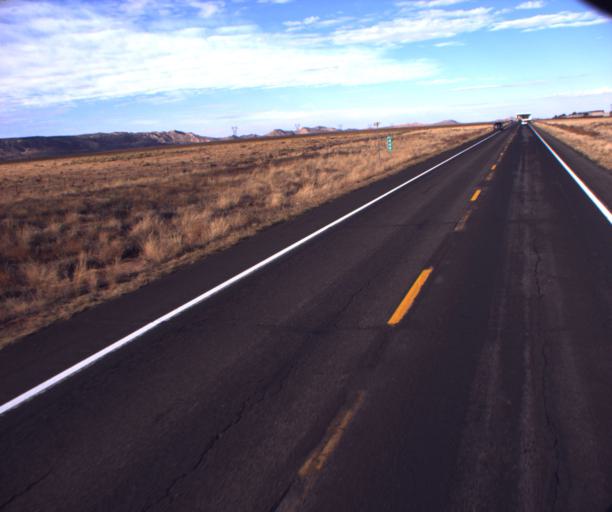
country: US
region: Arizona
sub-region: Apache County
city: Lukachukai
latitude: 36.9604
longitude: -109.3691
